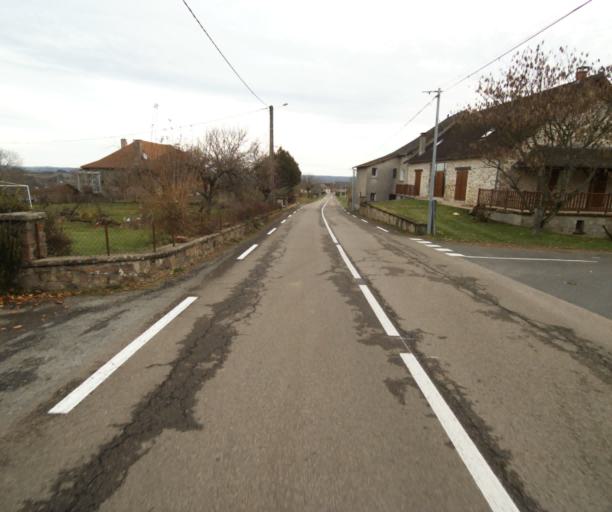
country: FR
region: Limousin
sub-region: Departement de la Correze
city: Chameyrat
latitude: 45.2661
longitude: 1.7178
